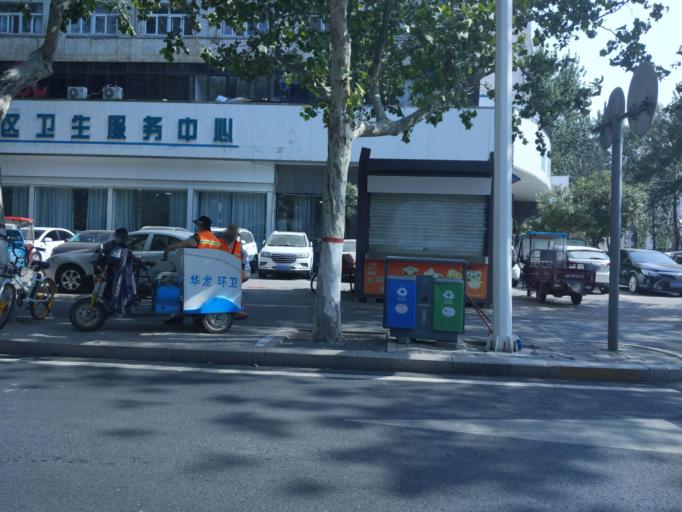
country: CN
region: Henan Sheng
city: Puyang
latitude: 35.7621
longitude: 115.0092
